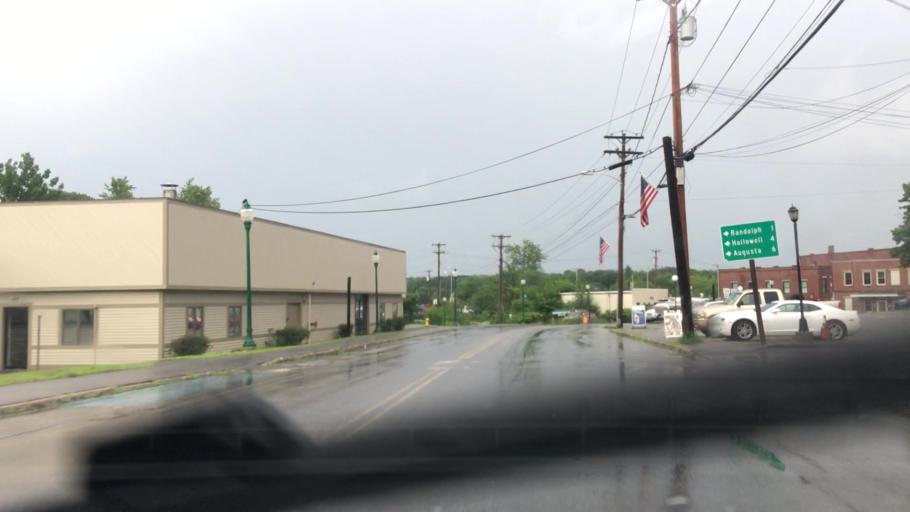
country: US
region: Maine
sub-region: Kennebec County
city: Gardiner
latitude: 44.2296
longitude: -69.7763
